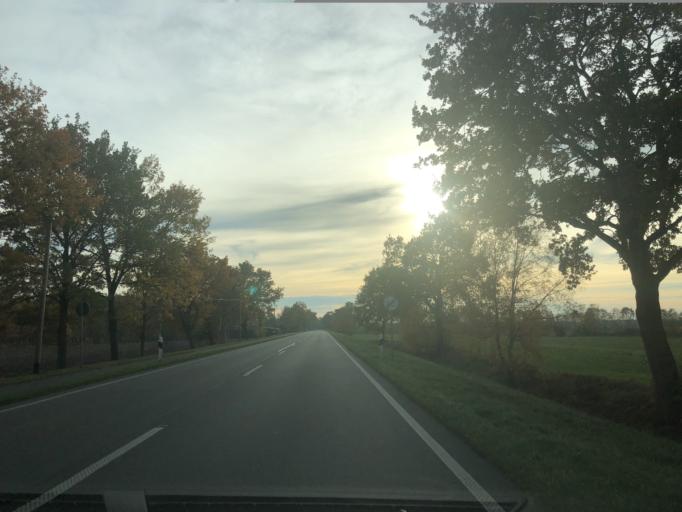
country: DE
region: Lower Saxony
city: Bosel
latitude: 53.0657
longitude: 7.9202
